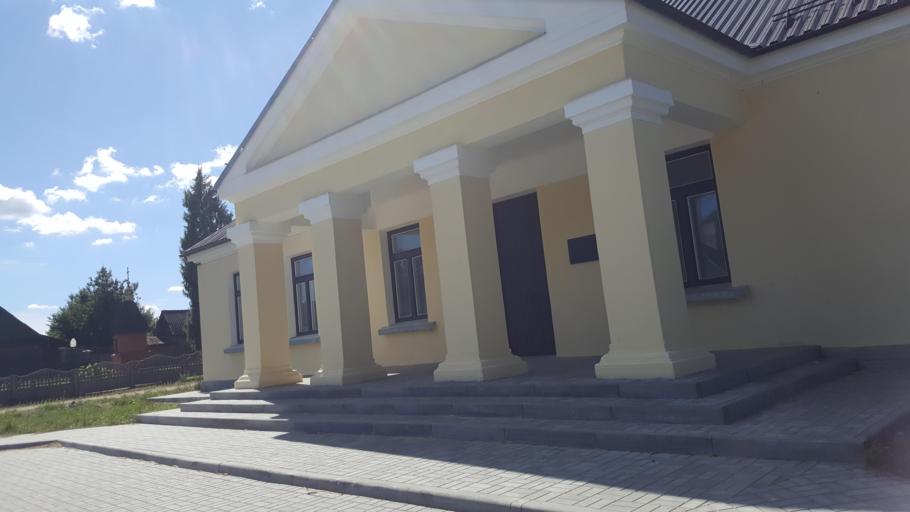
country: BY
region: Brest
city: Vysokaye
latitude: 52.2846
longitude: 23.3110
